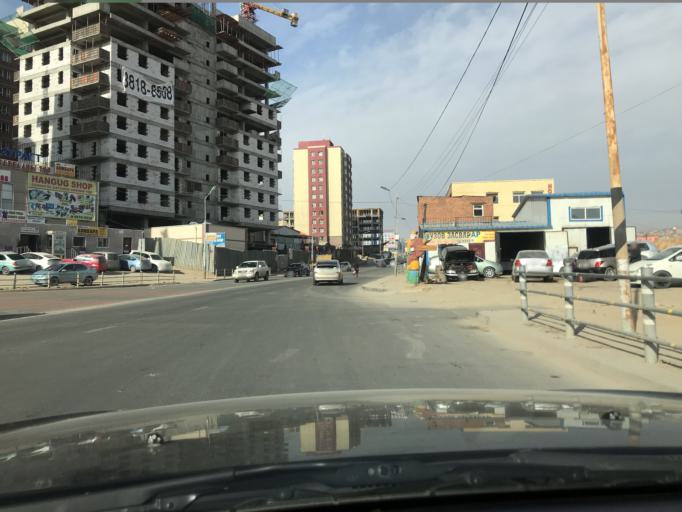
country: MN
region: Ulaanbaatar
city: Ulaanbaatar
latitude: 47.9255
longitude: 106.8959
